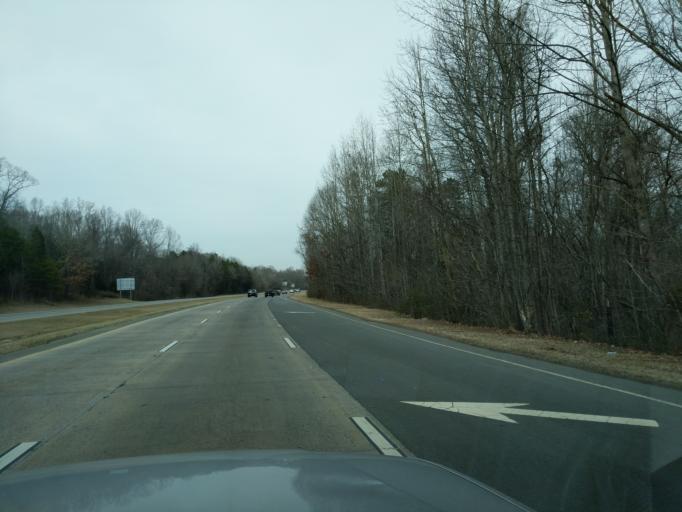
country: US
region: North Carolina
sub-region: Mecklenburg County
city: Charlotte
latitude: 35.1978
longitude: -80.9211
